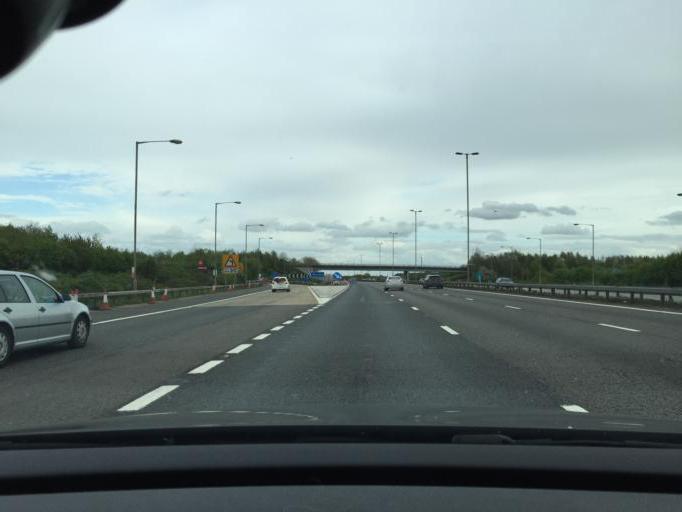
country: GB
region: England
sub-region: West Berkshire
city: Calcot
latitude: 51.4245
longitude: -1.0345
